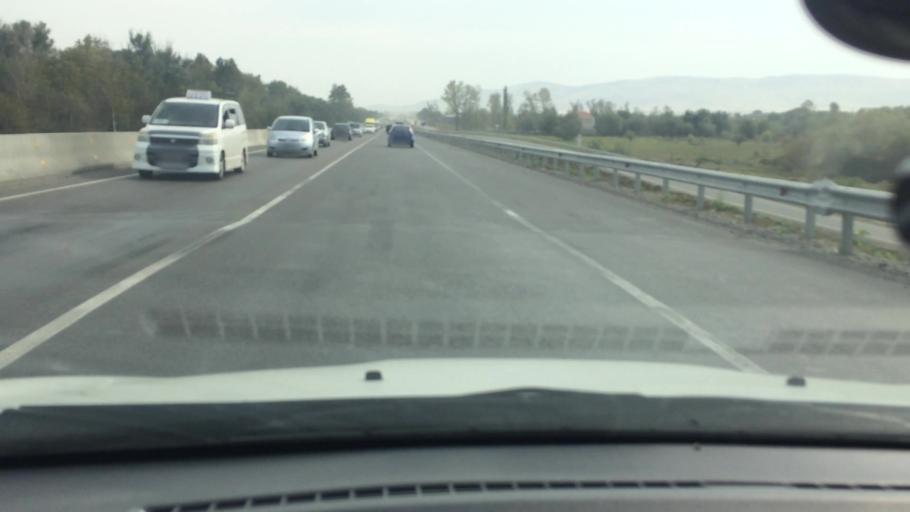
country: GE
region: Kvemo Kartli
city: Rust'avi
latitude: 41.6284
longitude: 44.9221
